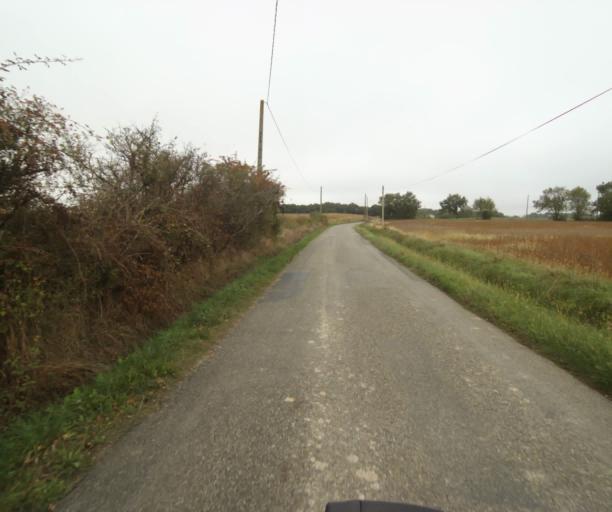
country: FR
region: Midi-Pyrenees
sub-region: Departement du Tarn-et-Garonne
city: Orgueil
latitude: 43.8913
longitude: 1.3850
